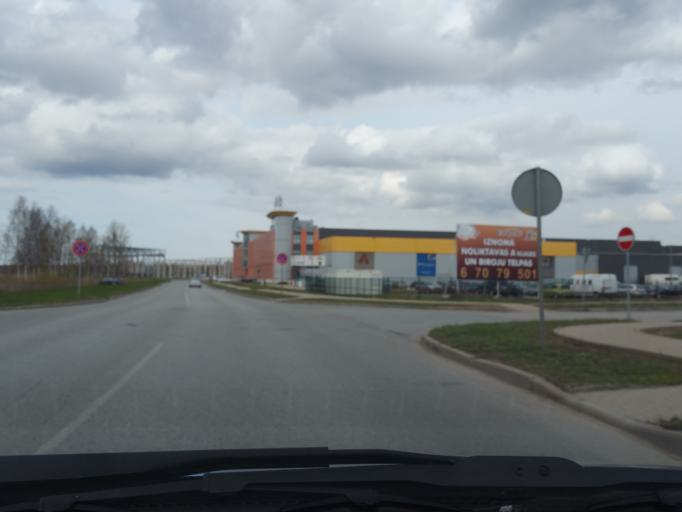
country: LV
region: Marupe
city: Marupe
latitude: 56.9234
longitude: 23.9930
